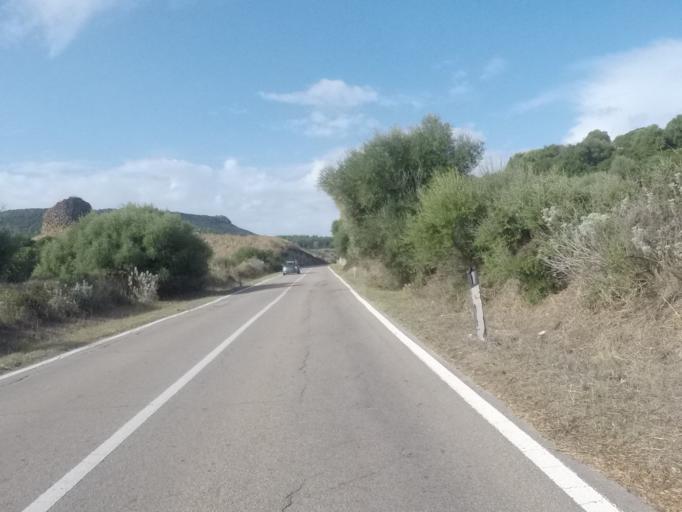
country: IT
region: Sardinia
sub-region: Provincia di Sassari
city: Castelsardo
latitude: 40.8942
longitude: 8.7559
